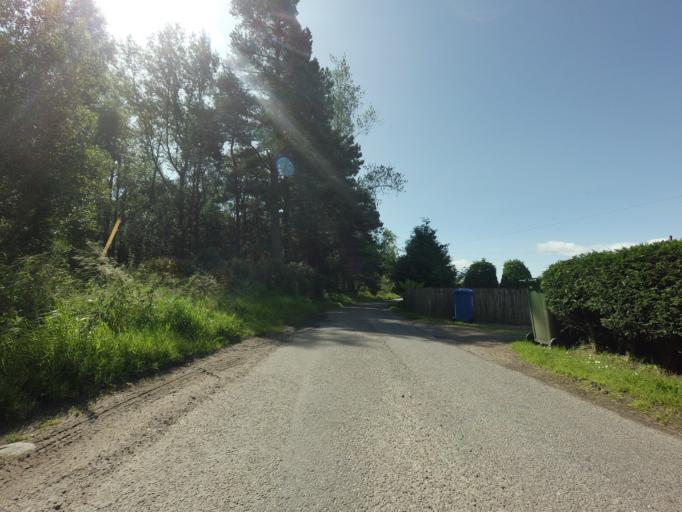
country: GB
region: Scotland
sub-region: Highland
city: Nairn
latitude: 57.5269
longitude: -3.8626
